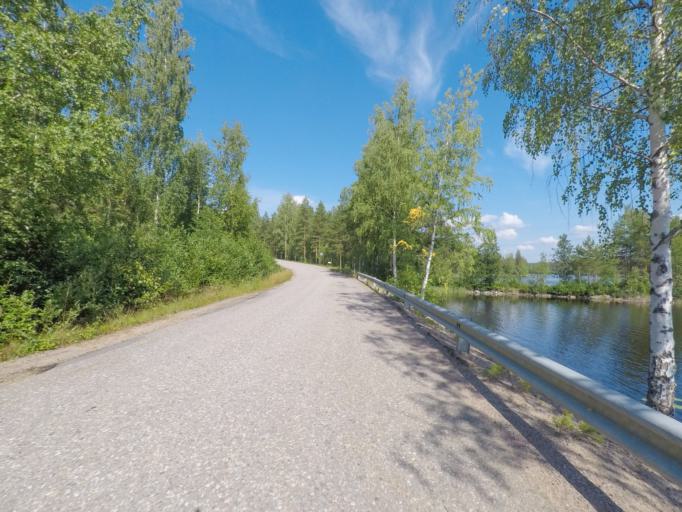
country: FI
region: Southern Savonia
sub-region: Mikkeli
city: Puumala
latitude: 61.4098
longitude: 28.0918
